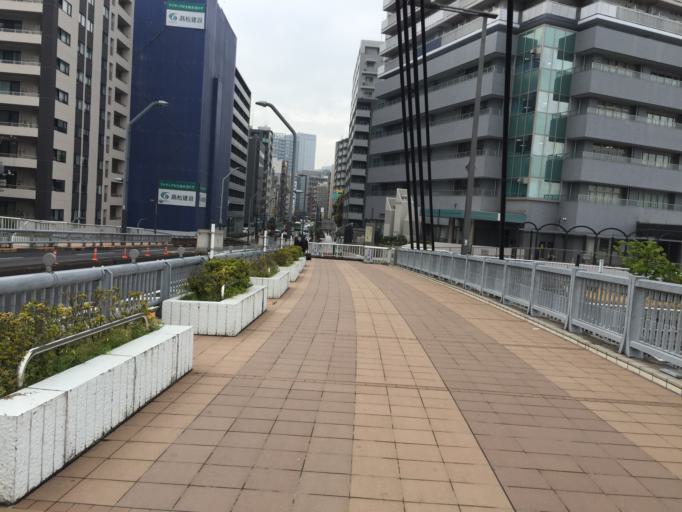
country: JP
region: Tokyo
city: Tokyo
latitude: 35.6724
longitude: 139.7842
